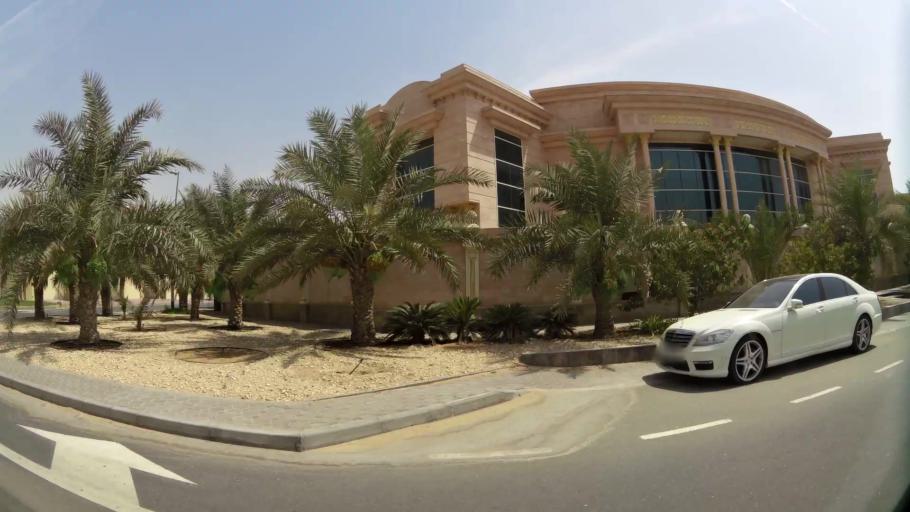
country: AE
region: Ash Shariqah
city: Sharjah
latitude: 25.2593
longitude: 55.4740
